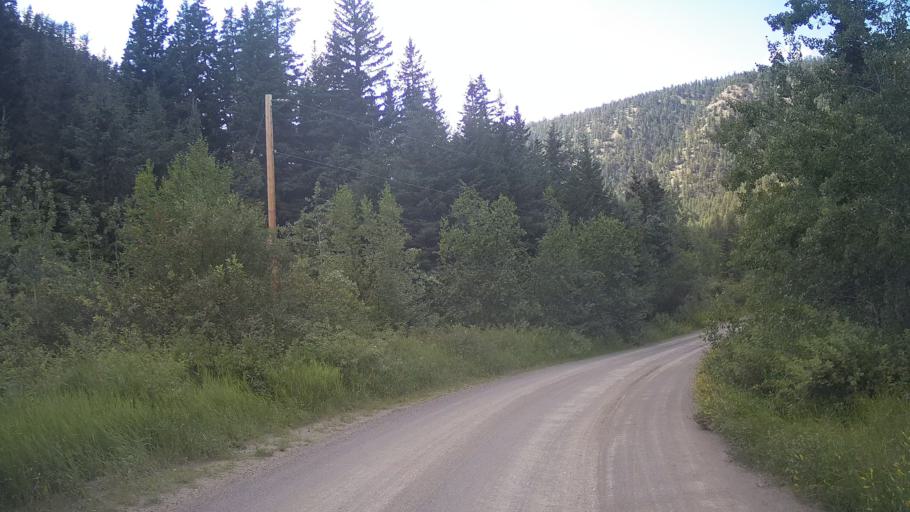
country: CA
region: British Columbia
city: Lillooet
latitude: 51.2513
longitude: -122.0148
